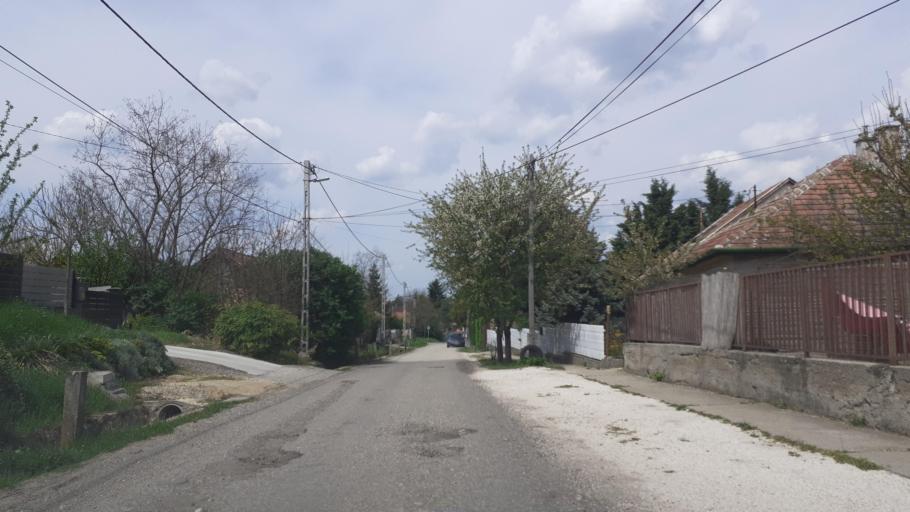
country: HU
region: Pest
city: Pecel
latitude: 47.4762
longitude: 19.3479
